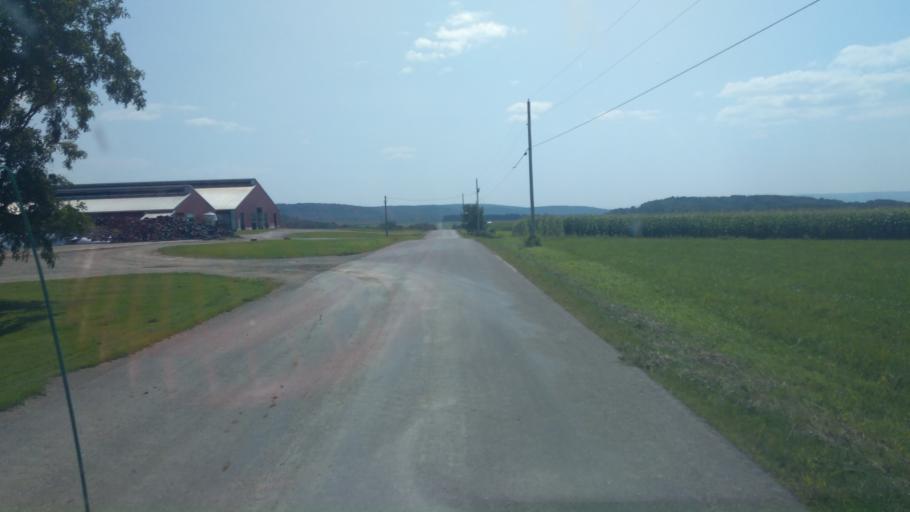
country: US
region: New York
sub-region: Steuben County
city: Canisteo
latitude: 42.3490
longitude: -77.5775
